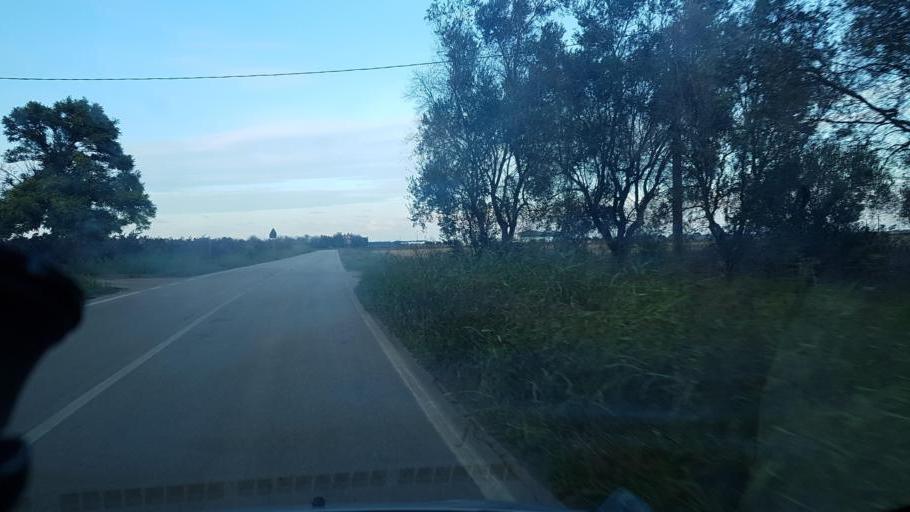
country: IT
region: Apulia
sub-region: Provincia di Lecce
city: Guagnano
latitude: 40.4300
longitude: 17.9496
